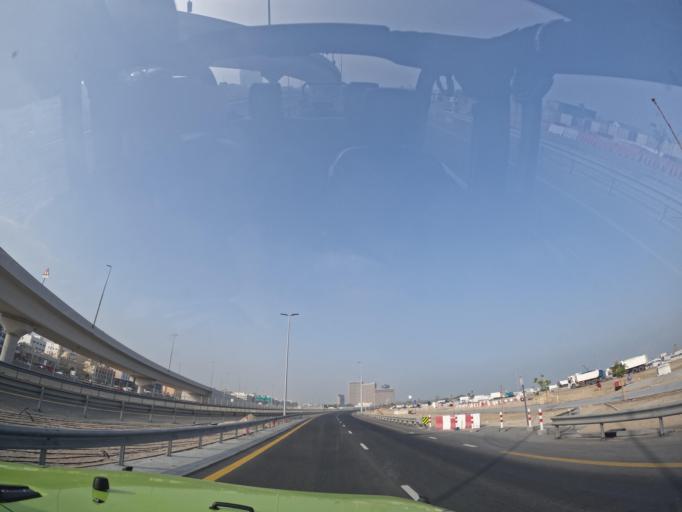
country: AE
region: Ash Shariqah
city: Sharjah
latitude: 25.2829
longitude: 55.3141
